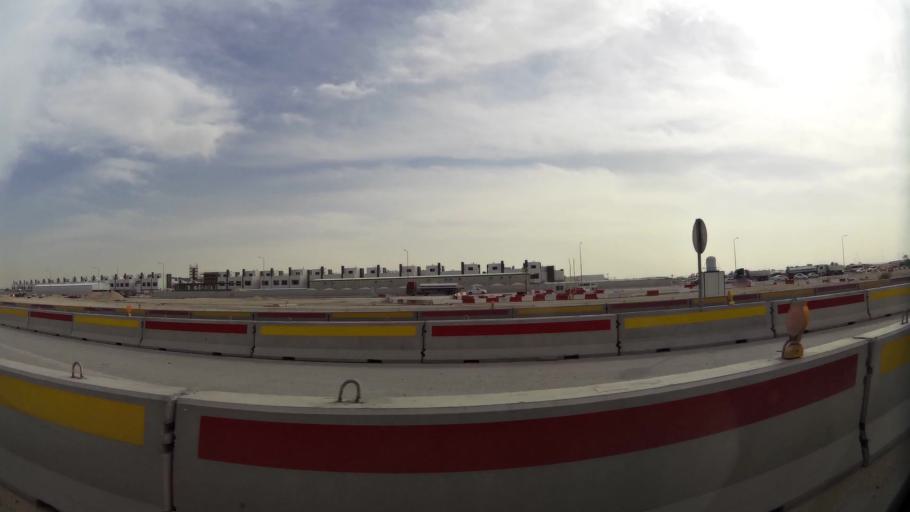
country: QA
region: Baladiyat ar Rayyan
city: Ar Rayyan
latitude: 25.3275
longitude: 51.3381
